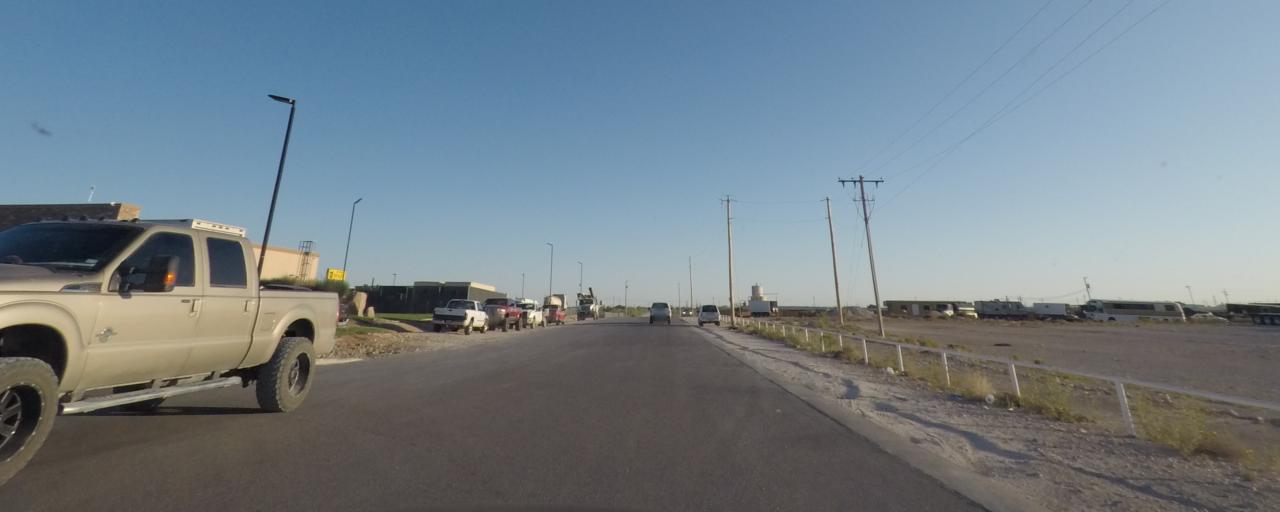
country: US
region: New Mexico
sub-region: Lea County
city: Hobbs
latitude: 32.6969
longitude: -103.1830
